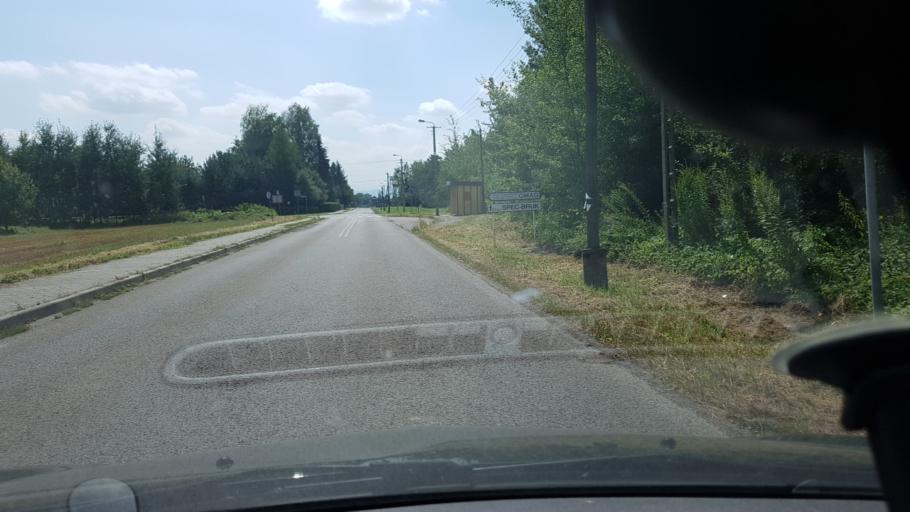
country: PL
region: Lesser Poland Voivodeship
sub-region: Powiat oswiecimski
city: Brzezinka
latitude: 50.0438
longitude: 19.1814
